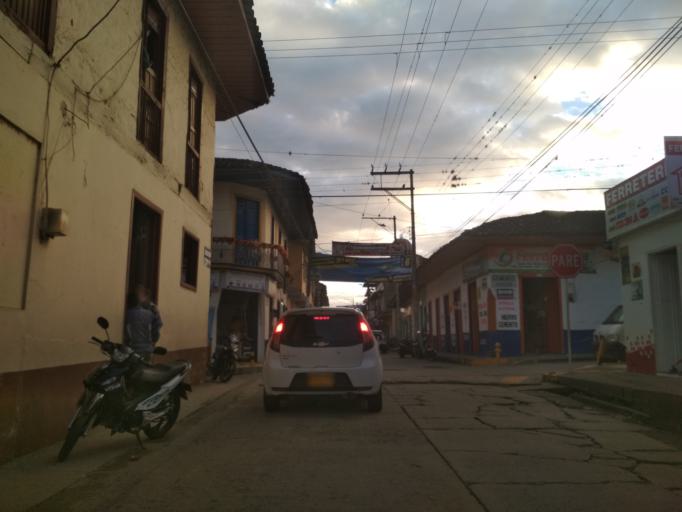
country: CO
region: Valle del Cauca
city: Calimita
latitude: 3.9331
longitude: -76.4839
